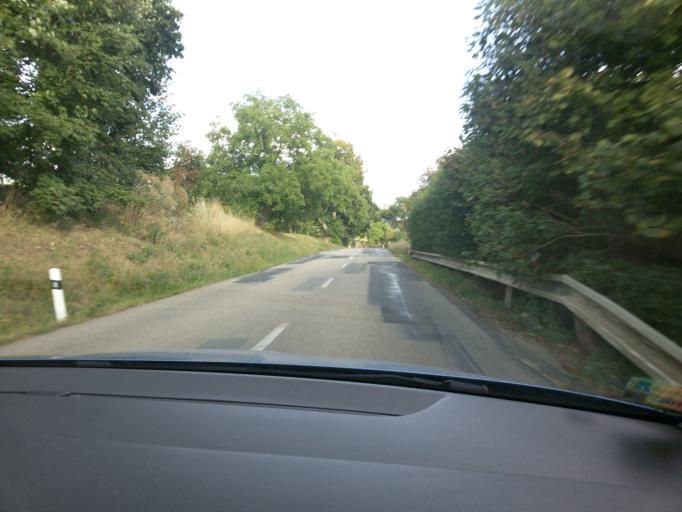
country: CZ
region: South Moravian
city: Olesnice
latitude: 49.5462
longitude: 16.4334
